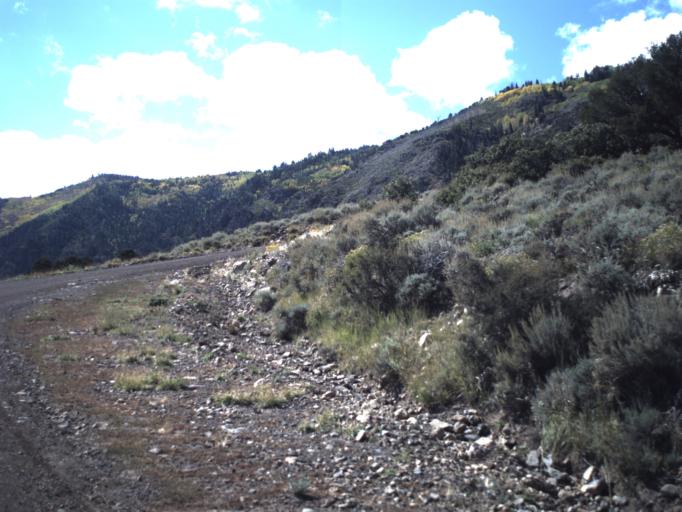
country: US
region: Utah
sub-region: Piute County
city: Junction
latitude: 38.2548
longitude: -112.3175
